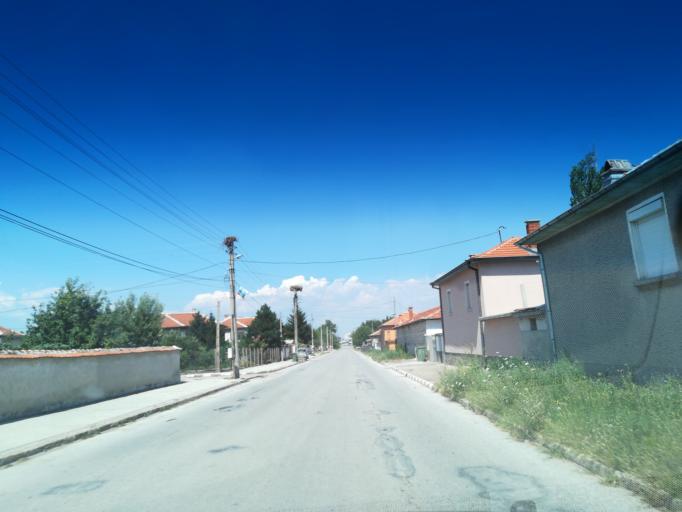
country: BG
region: Plovdiv
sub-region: Obshtina Sadovo
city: Sadovo
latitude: 42.0306
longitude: 25.1150
